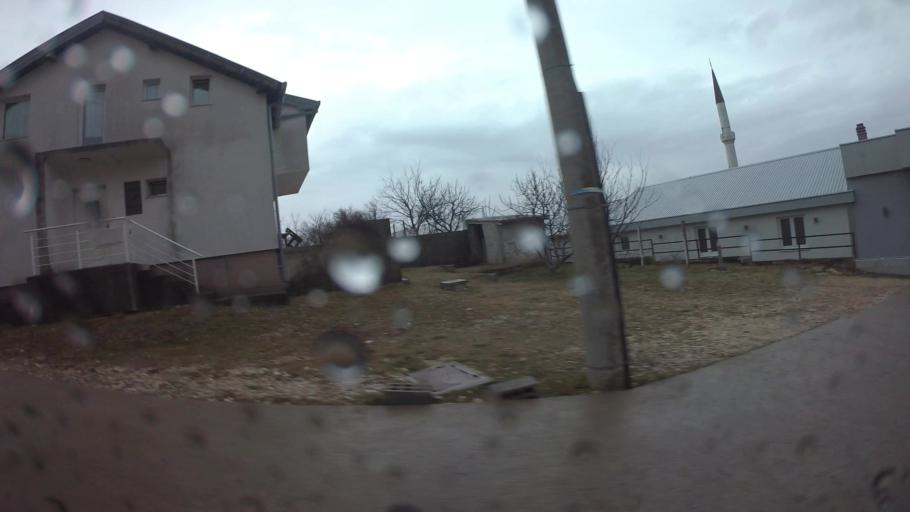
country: BA
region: Federation of Bosnia and Herzegovina
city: Rodoc
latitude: 43.3172
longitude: 17.8364
